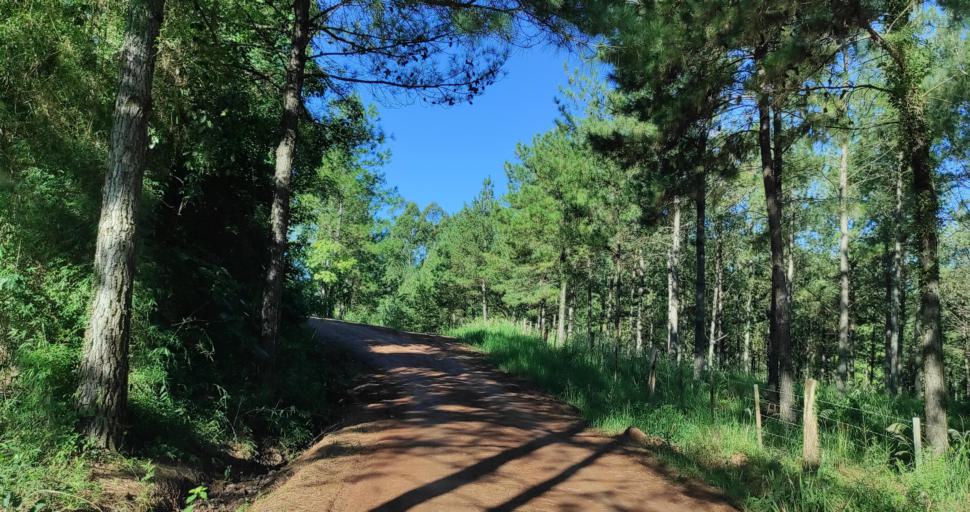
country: AR
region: Misiones
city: Capiovi
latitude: -26.9075
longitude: -54.9971
